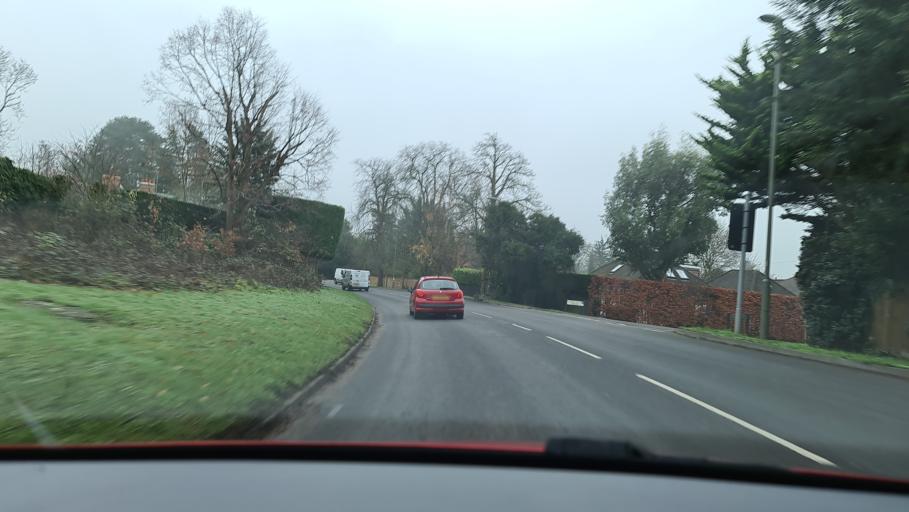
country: GB
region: England
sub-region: Surrey
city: Leatherhead
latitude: 51.3263
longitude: -0.3544
